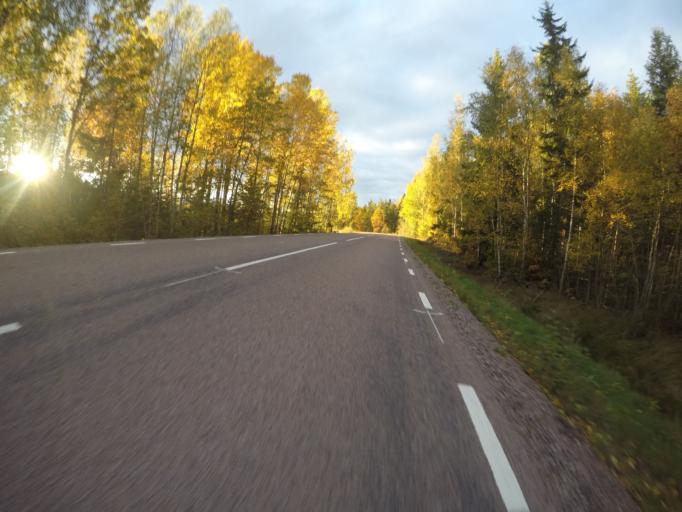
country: SE
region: Vaestmanland
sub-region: Arboga Kommun
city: Tyringe
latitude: 59.3091
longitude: 15.9936
